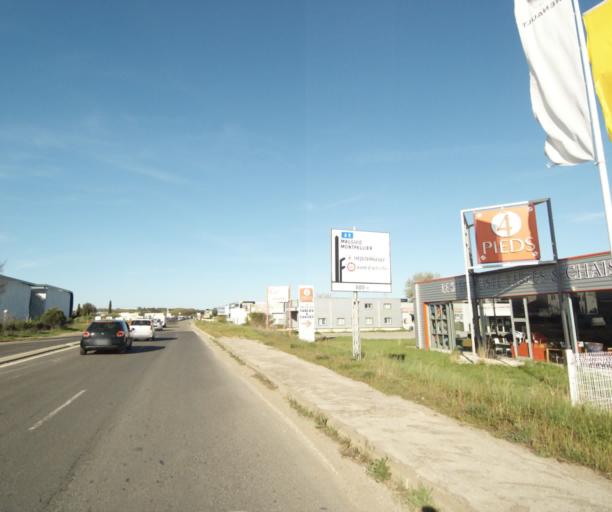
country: FR
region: Languedoc-Roussillon
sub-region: Departement de l'Herault
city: Perols
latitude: 43.5906
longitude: 3.9354
